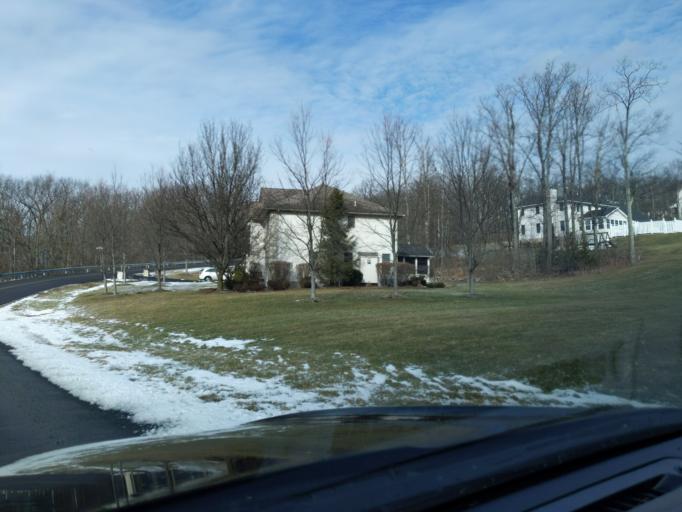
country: US
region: Pennsylvania
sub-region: Blair County
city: Lakemont
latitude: 40.4736
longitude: -78.3781
